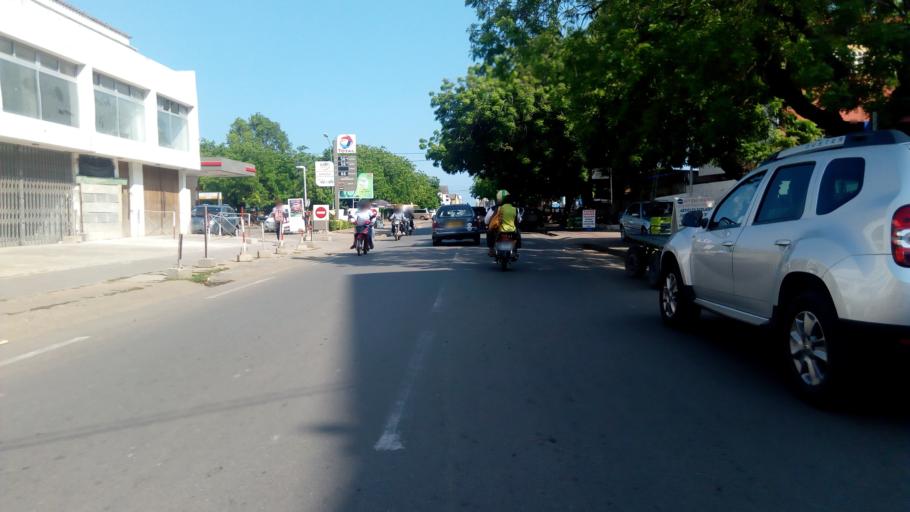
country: TG
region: Maritime
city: Lome
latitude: 6.1326
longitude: 1.2233
